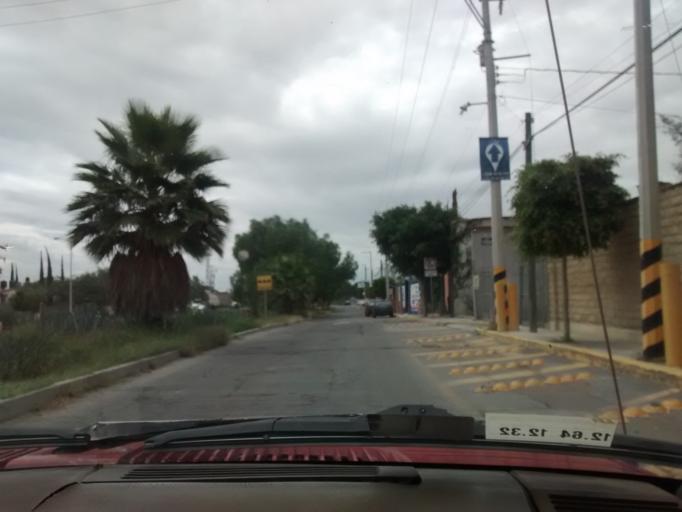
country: MX
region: Puebla
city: Tehuacan
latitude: 18.4797
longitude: -97.4114
